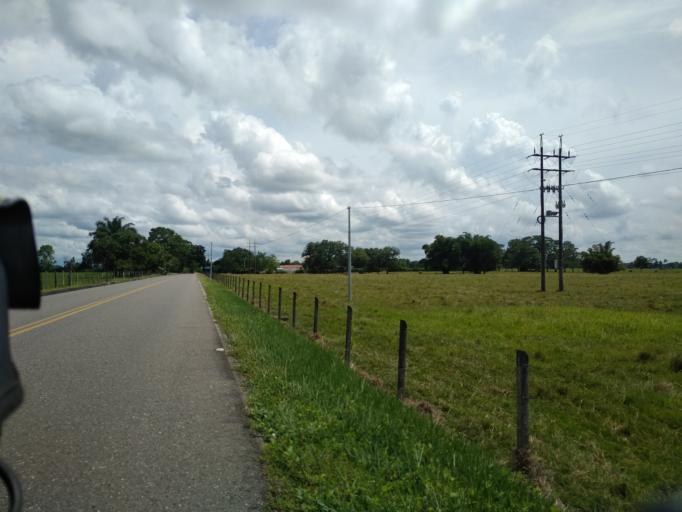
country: CO
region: Santander
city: Puerto Parra
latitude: 6.5067
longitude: -74.0614
